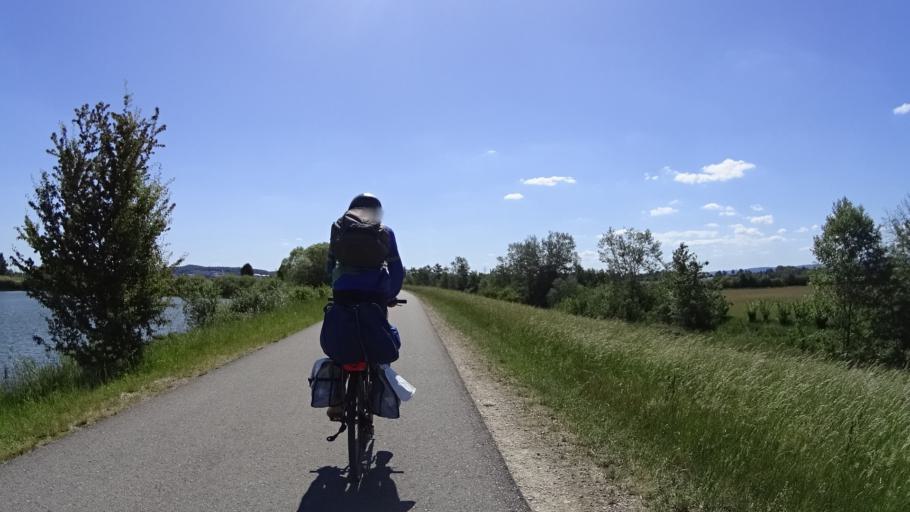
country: DE
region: Bavaria
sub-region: Regierungsbezirk Mittelfranken
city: Gunzenhausen
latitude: 49.1204
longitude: 10.7280
